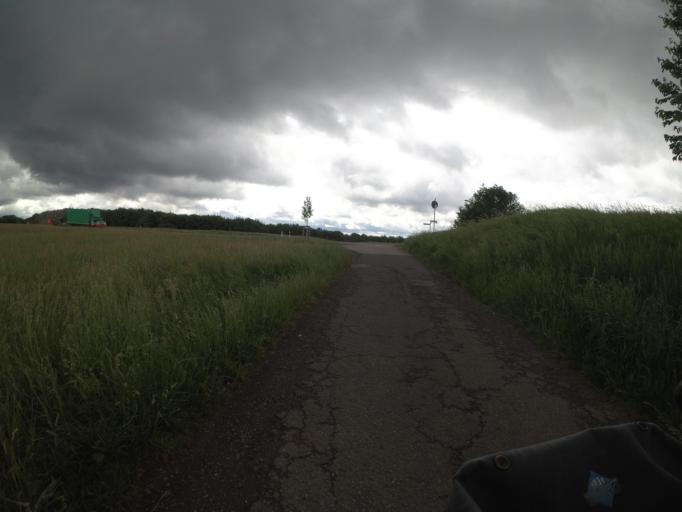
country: DE
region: Rheinland-Pfalz
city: Obersimten
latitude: 49.1622
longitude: 7.6047
